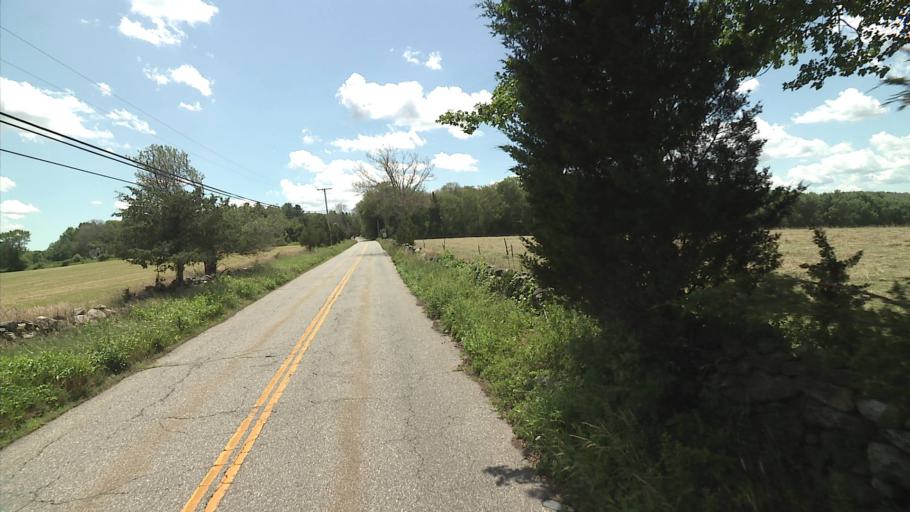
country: US
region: Connecticut
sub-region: New London County
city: Preston City
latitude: 41.5367
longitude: -71.8807
